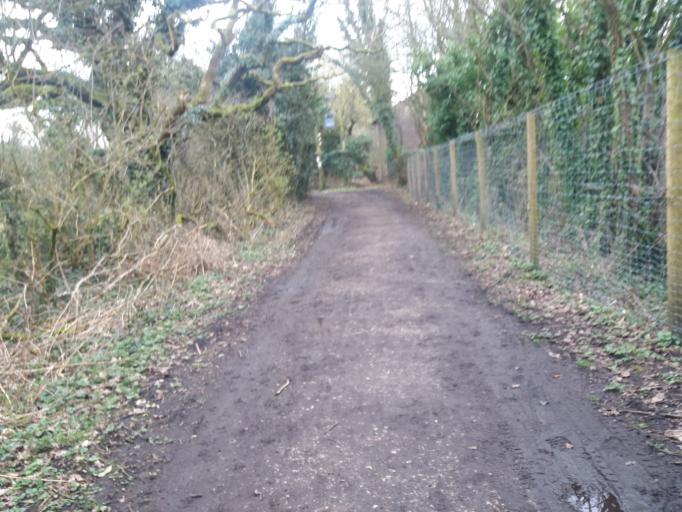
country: GB
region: England
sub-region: Lancashire
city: Chorley
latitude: 53.6578
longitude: -2.6081
